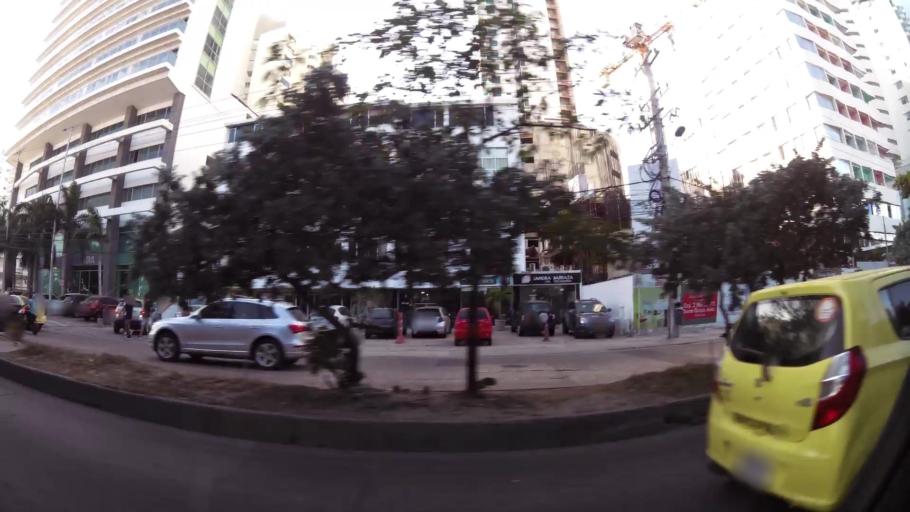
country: CO
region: Bolivar
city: Cartagena
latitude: 10.4090
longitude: -75.5507
